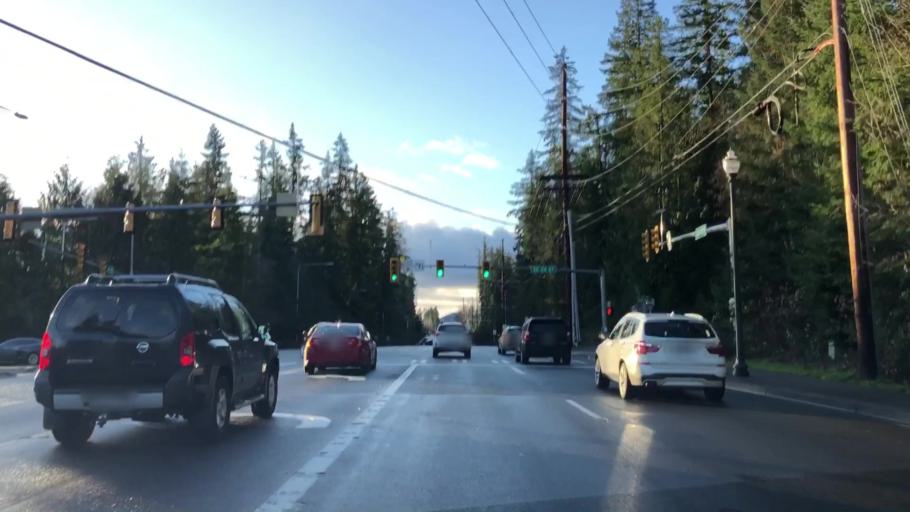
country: US
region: Washington
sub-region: King County
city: City of Sammamish
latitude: 47.5887
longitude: -122.0355
